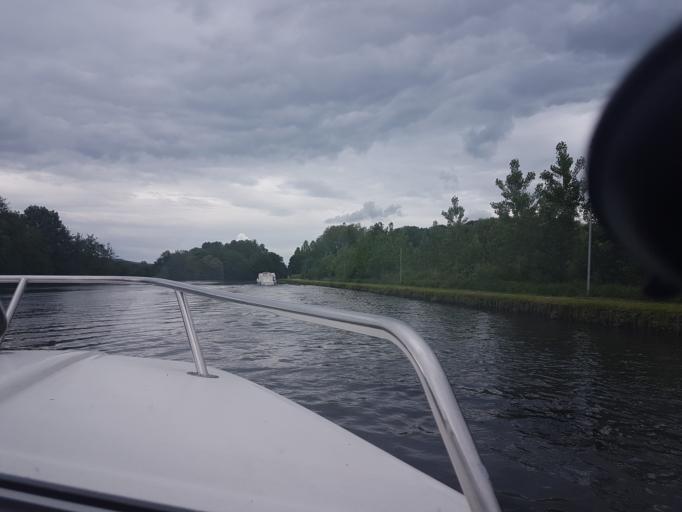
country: FR
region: Bourgogne
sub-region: Departement de l'Yonne
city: Champs-sur-Yonne
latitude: 47.7297
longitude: 3.6043
